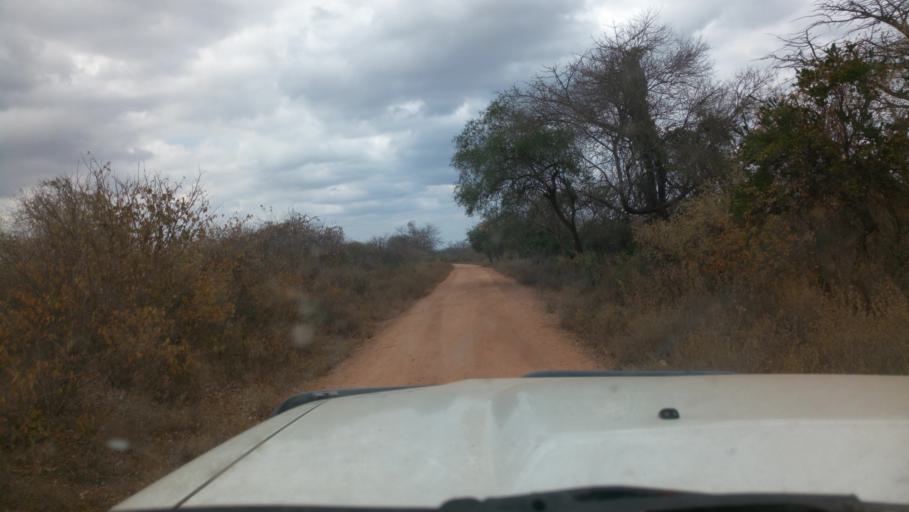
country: KE
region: Kitui
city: Kitui
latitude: -1.8899
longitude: 38.4038
